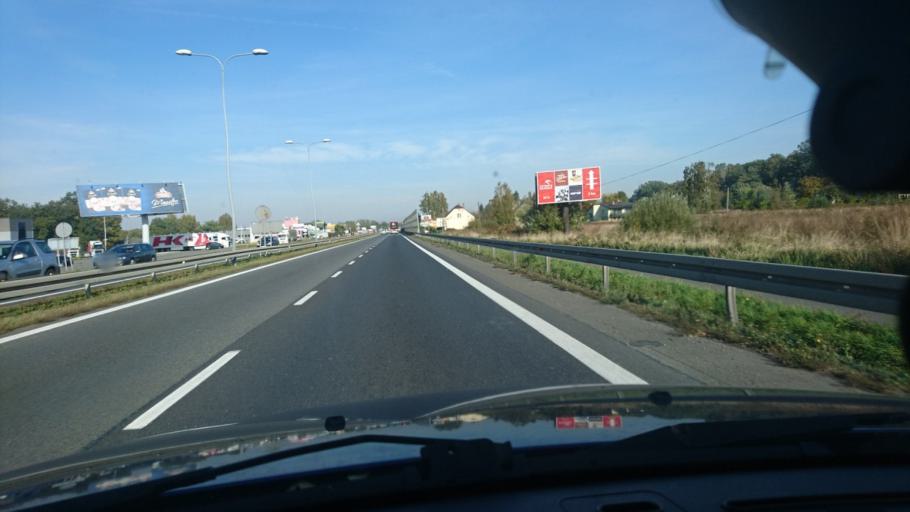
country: PL
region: Silesian Voivodeship
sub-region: Powiat pszczynski
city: Goczalkowice Zdroj
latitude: 49.9572
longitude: 18.9647
